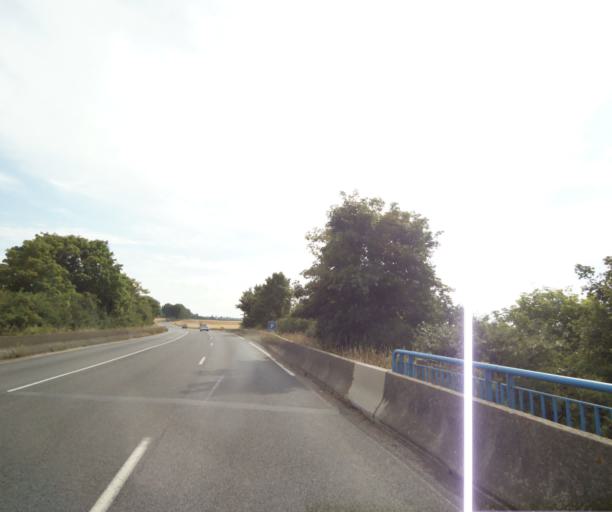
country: FR
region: Ile-de-France
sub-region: Departement de Seine-et-Marne
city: La Chapelle-la-Reine
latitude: 48.3363
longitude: 2.5948
